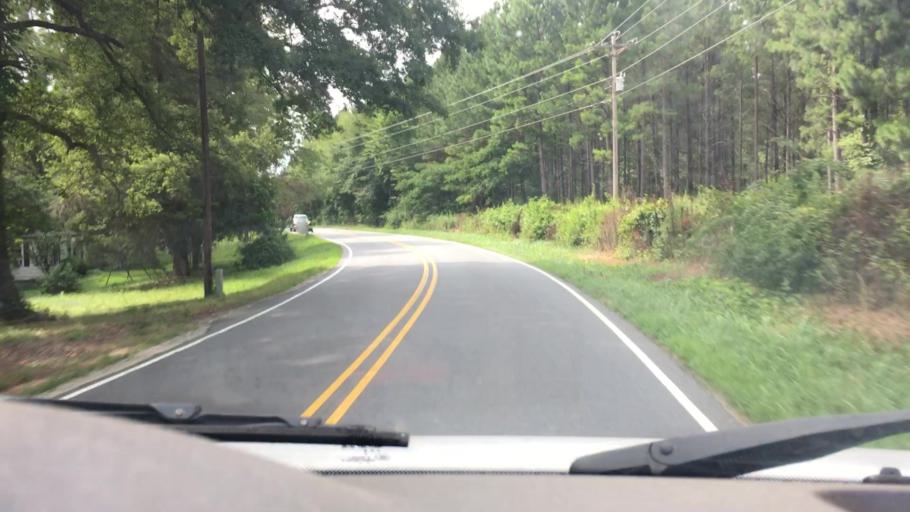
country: US
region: North Carolina
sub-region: Gaston County
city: Davidson
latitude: 35.4804
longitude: -80.8055
